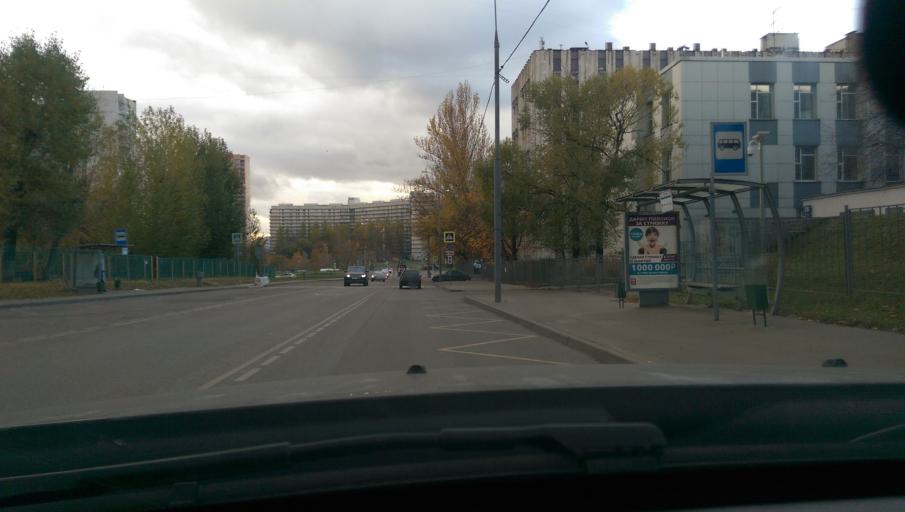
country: RU
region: Moscow
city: Kotlovka
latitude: 55.6442
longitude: 37.5946
